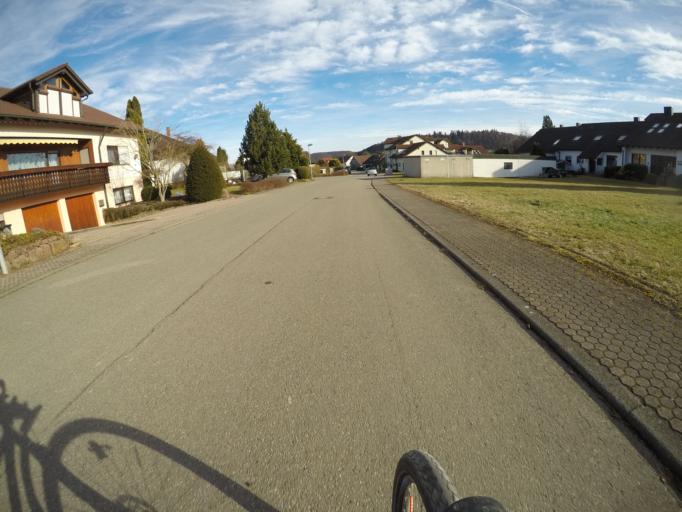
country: DE
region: Baden-Wuerttemberg
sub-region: Regierungsbezirk Stuttgart
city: Nufringen
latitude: 48.6224
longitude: 8.8805
